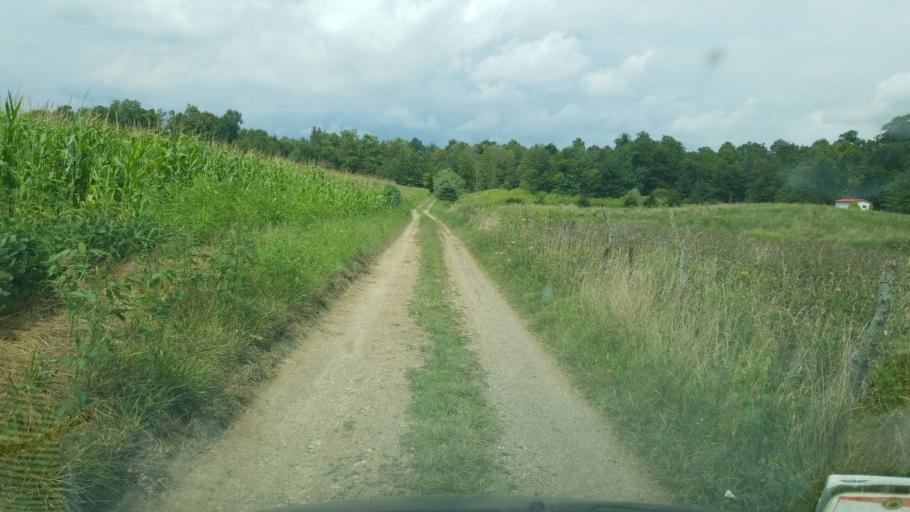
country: US
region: Ohio
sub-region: Morrow County
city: Mount Gilead
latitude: 40.5070
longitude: -82.7180
